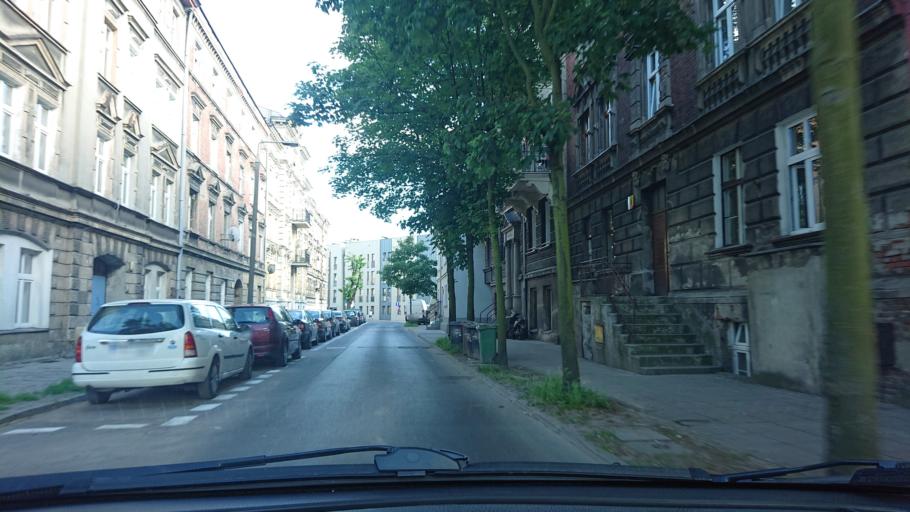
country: PL
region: Greater Poland Voivodeship
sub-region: Powiat gnieznienski
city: Gniezno
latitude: 52.5312
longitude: 17.5923
